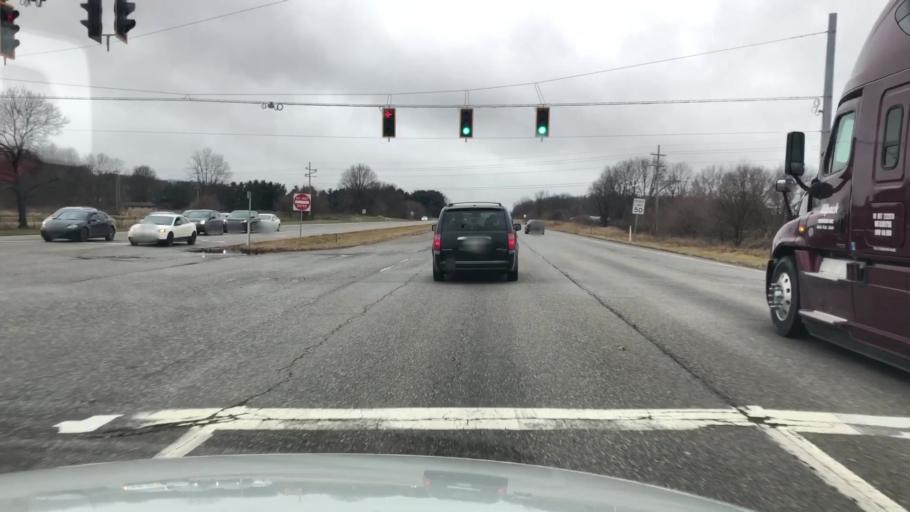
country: US
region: Indiana
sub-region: Marshall County
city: Plymouth
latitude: 41.3423
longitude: -86.2621
